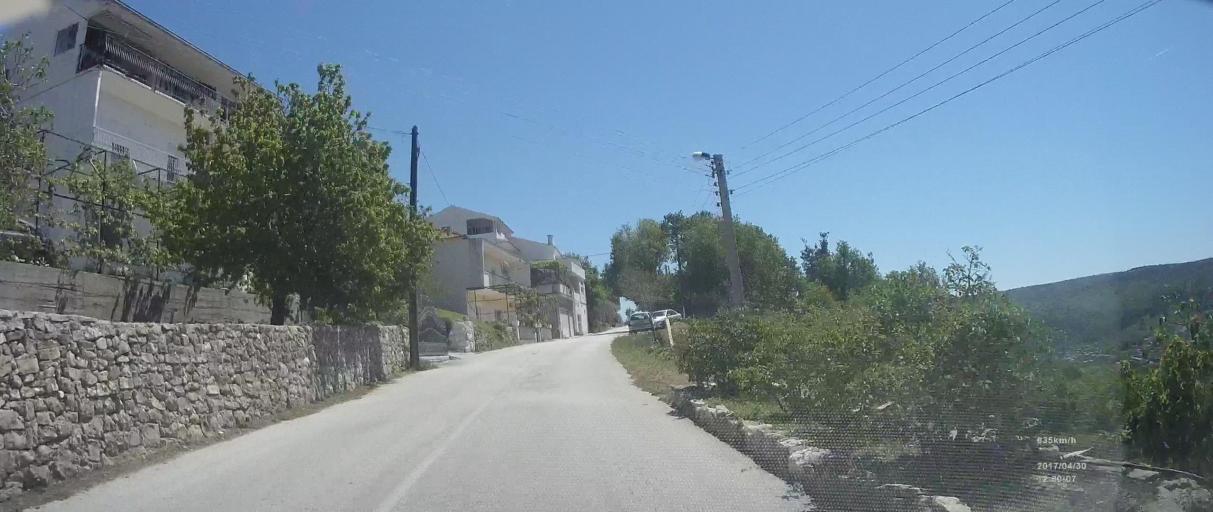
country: HR
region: Splitsko-Dalmatinska
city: Srinjine
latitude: 43.5010
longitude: 16.6038
